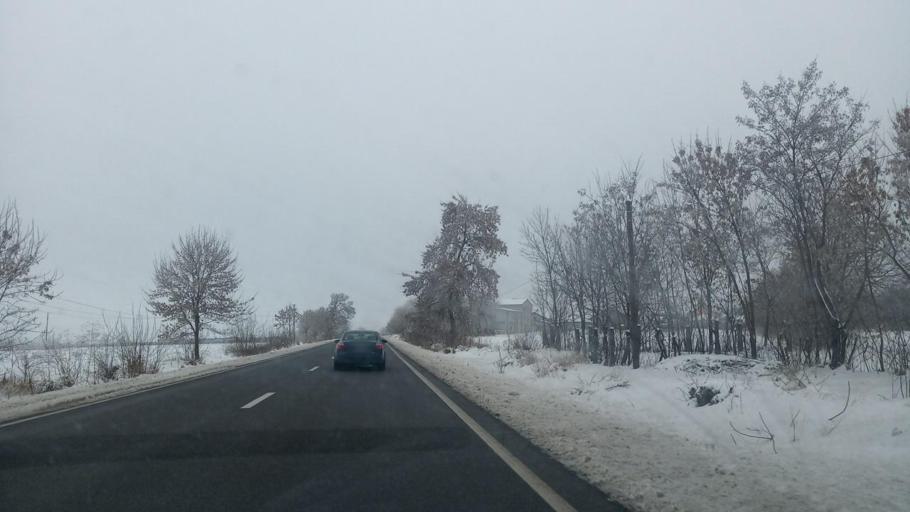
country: RO
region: Iasi
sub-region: Comuna Mircesti
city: Iugani
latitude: 47.0384
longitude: 26.8293
